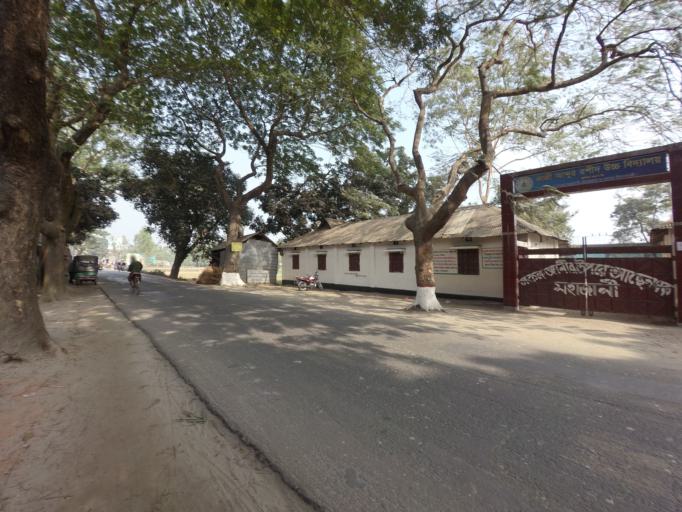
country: BD
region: Rajshahi
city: Saidpur
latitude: 25.8495
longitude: 88.8730
